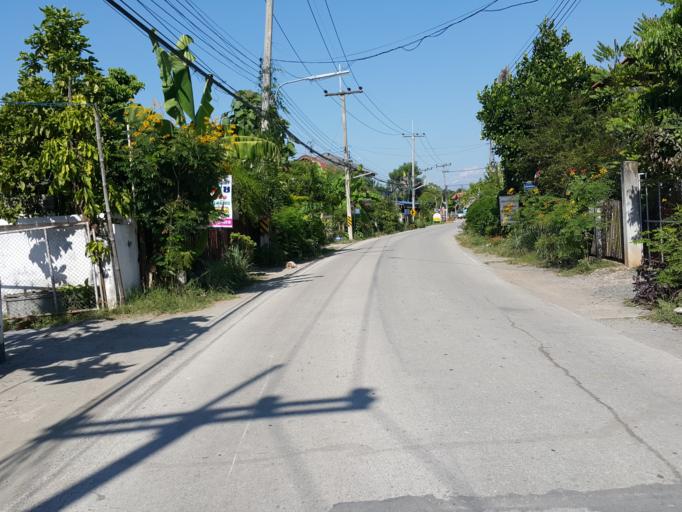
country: TH
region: Chiang Mai
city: San Kamphaeng
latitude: 18.7775
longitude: 99.1214
